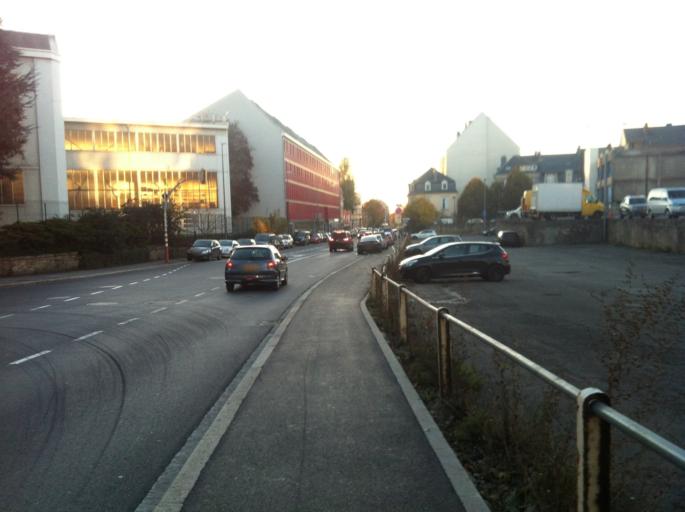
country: LU
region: Luxembourg
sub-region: Canton de Luxembourg
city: Luxembourg
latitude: 49.5982
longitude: 6.1311
